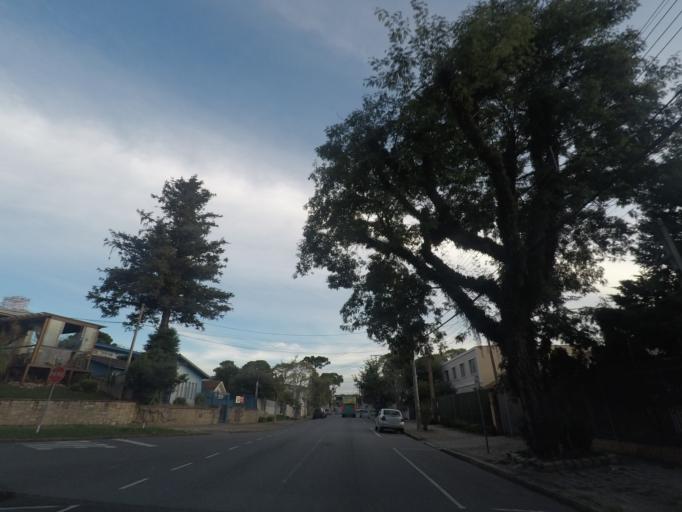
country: BR
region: Parana
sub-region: Curitiba
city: Curitiba
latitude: -25.4204
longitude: -49.2829
